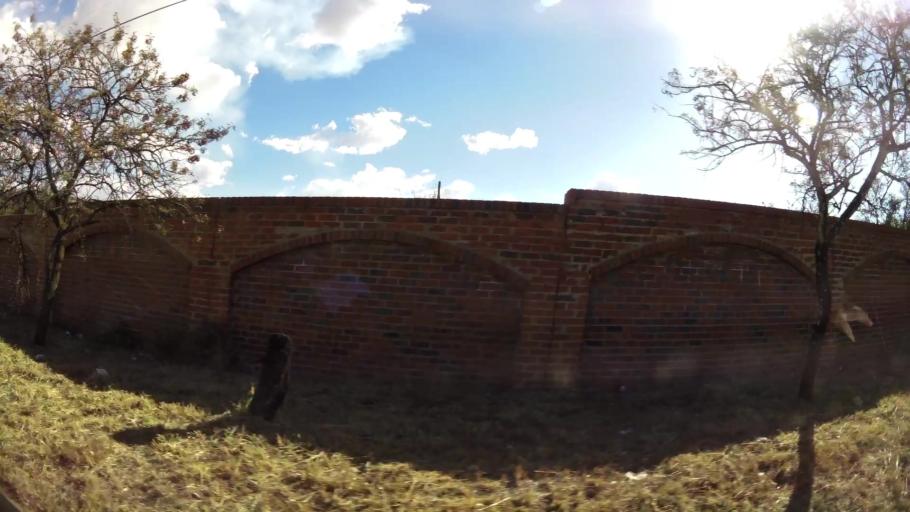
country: ZA
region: North-West
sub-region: Dr Kenneth Kaunda District Municipality
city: Klerksdorp
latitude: -26.8174
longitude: 26.6796
